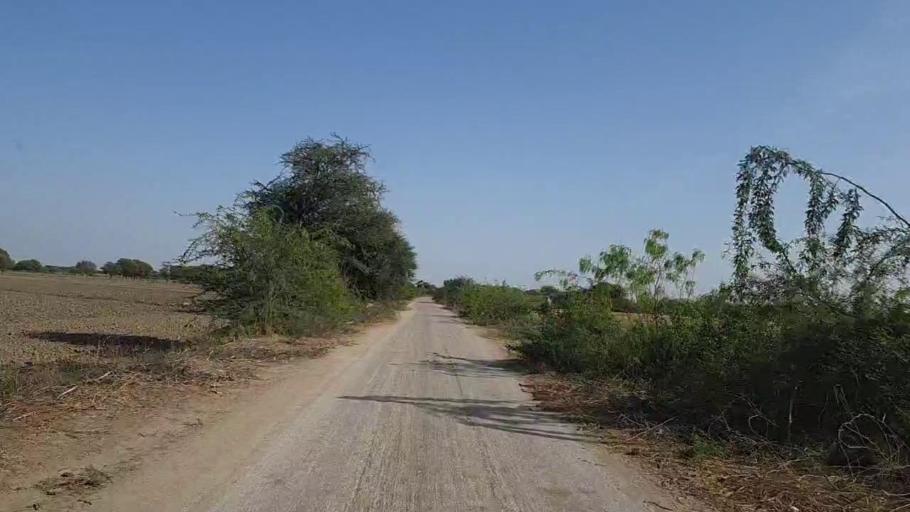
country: PK
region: Sindh
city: Kotri
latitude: 25.1477
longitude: 68.2951
